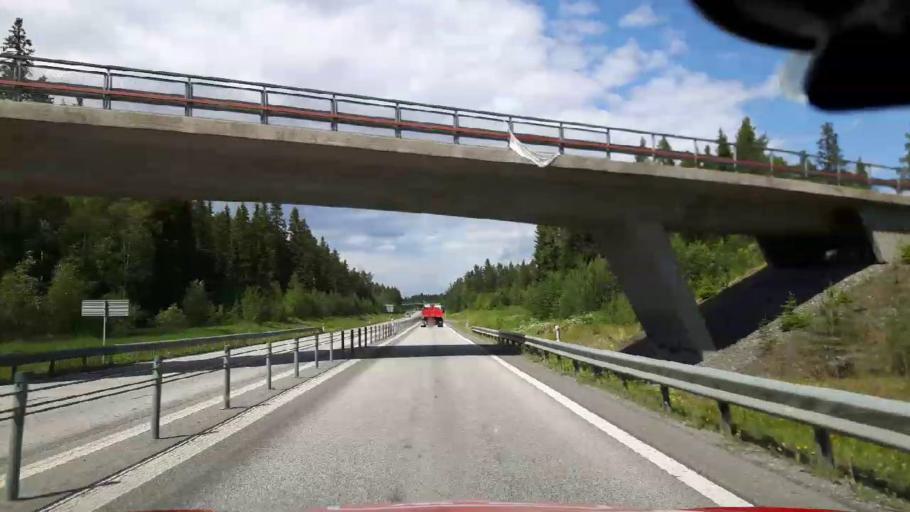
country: SE
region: Jaemtland
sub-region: OEstersunds Kommun
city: Ostersund
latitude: 63.2074
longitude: 14.6691
